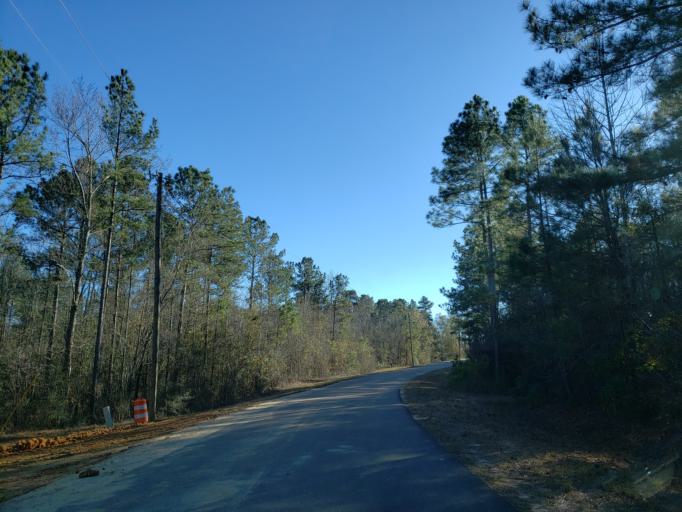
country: US
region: Mississippi
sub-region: Lamar County
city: Sumrall
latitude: 31.3559
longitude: -89.4758
